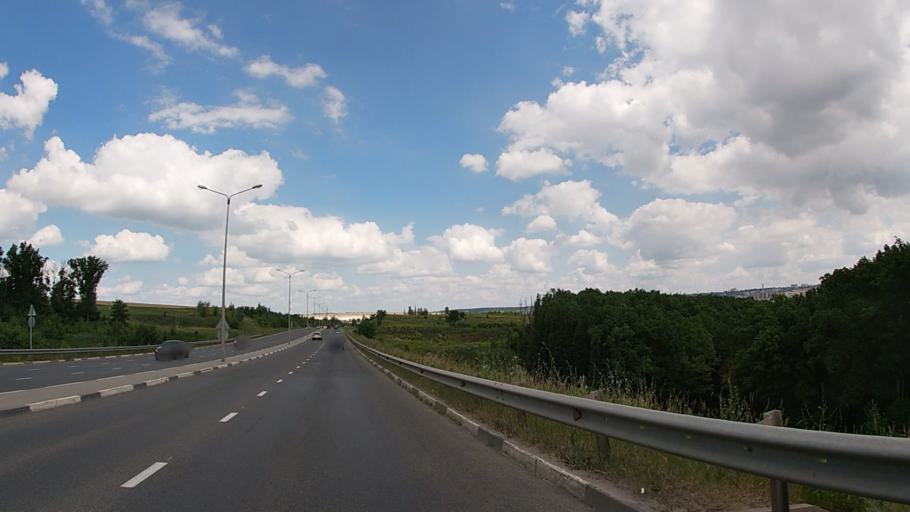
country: RU
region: Belgorod
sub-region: Belgorodskiy Rayon
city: Belgorod
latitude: 50.5998
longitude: 36.5302
